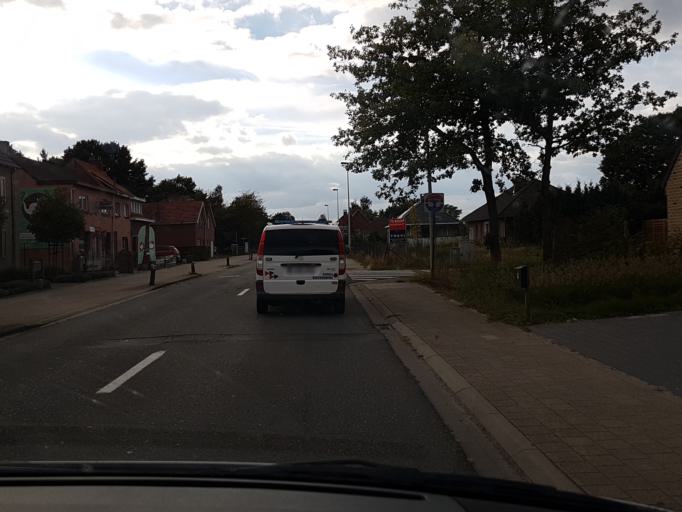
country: BE
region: Flanders
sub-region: Provincie Antwerpen
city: Schilde
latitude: 51.2113
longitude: 4.6096
